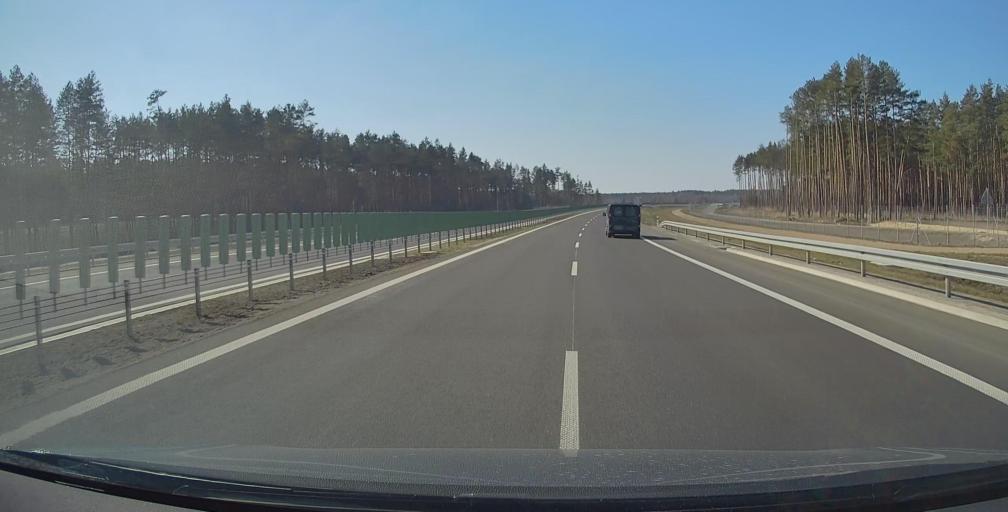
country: PL
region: Subcarpathian Voivodeship
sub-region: Powiat nizanski
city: Przedzel
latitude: 50.4794
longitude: 22.1845
